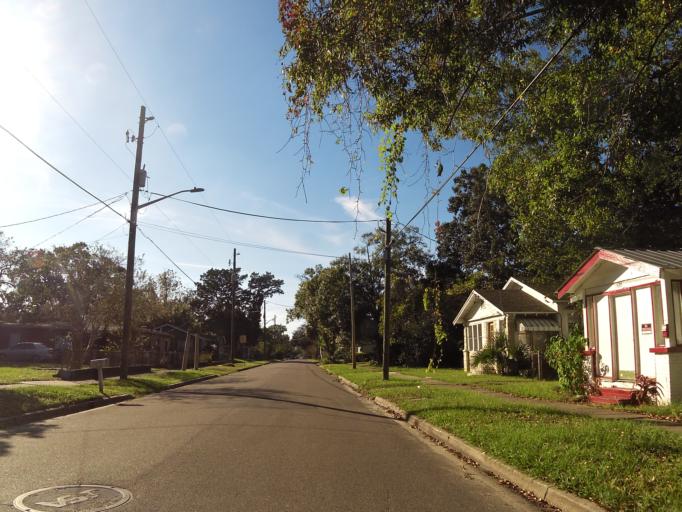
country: US
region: Florida
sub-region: Duval County
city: Jacksonville
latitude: 30.3527
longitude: -81.6784
